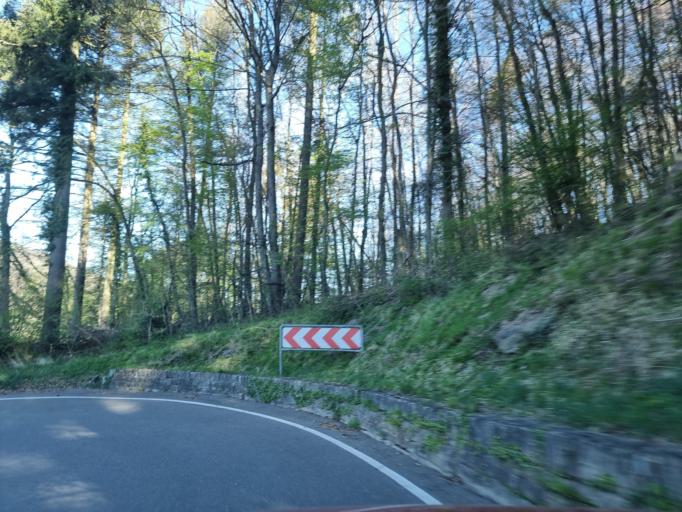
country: DE
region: Rheinland-Pfalz
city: Prumzurlay
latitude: 49.8689
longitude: 6.4399
